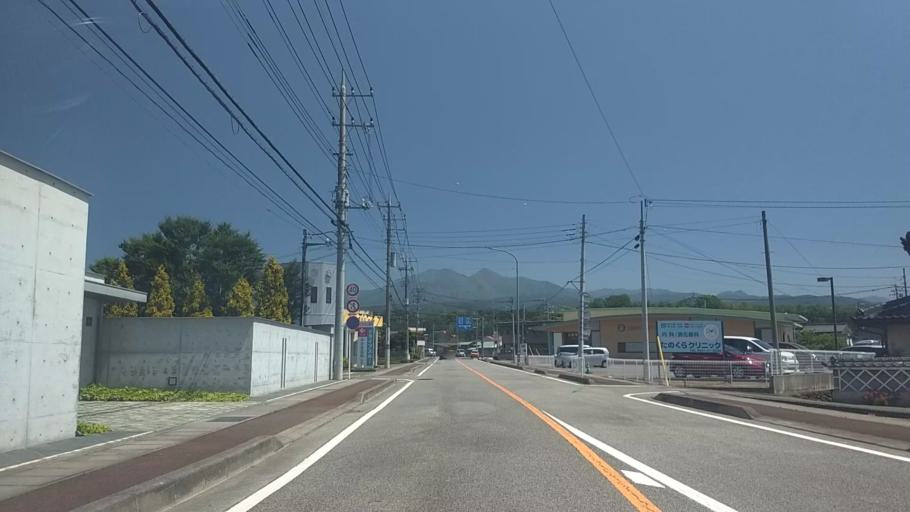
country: JP
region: Yamanashi
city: Nirasaki
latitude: 35.7193
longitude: 138.4498
